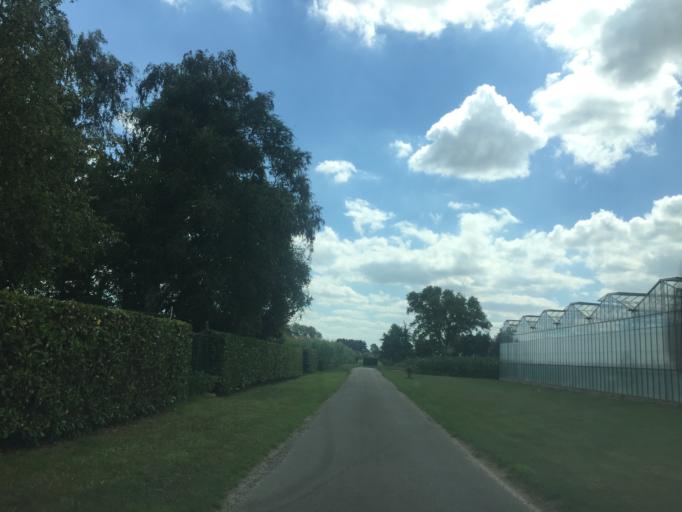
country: BE
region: Flanders
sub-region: Provincie West-Vlaanderen
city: Kortemark
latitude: 50.9997
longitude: 3.0405
